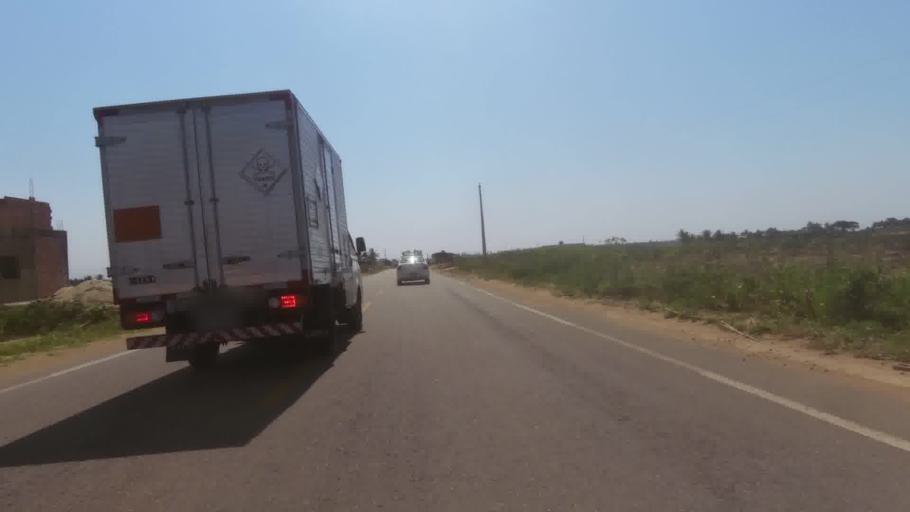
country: BR
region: Espirito Santo
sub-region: Marataizes
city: Marataizes
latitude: -21.0637
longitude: -40.8504
